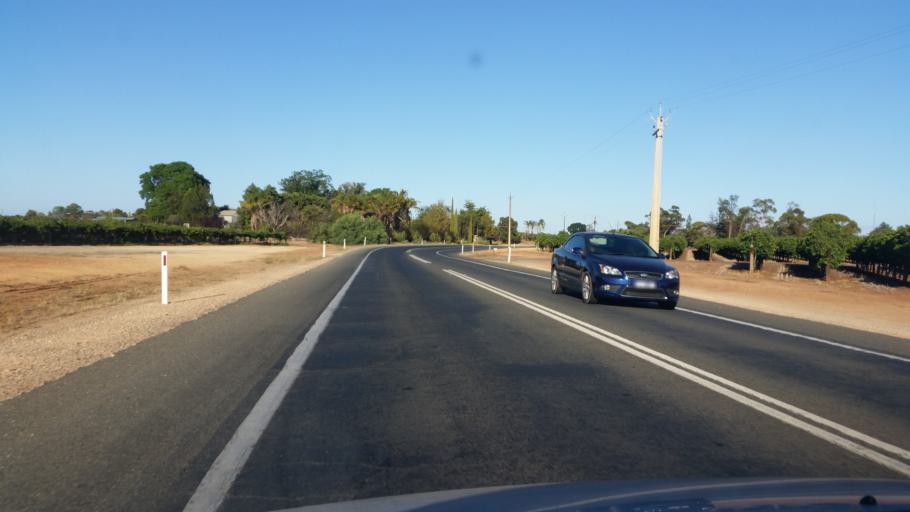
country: AU
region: South Australia
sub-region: Berri and Barmera
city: Barmera
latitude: -34.2655
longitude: 140.4989
